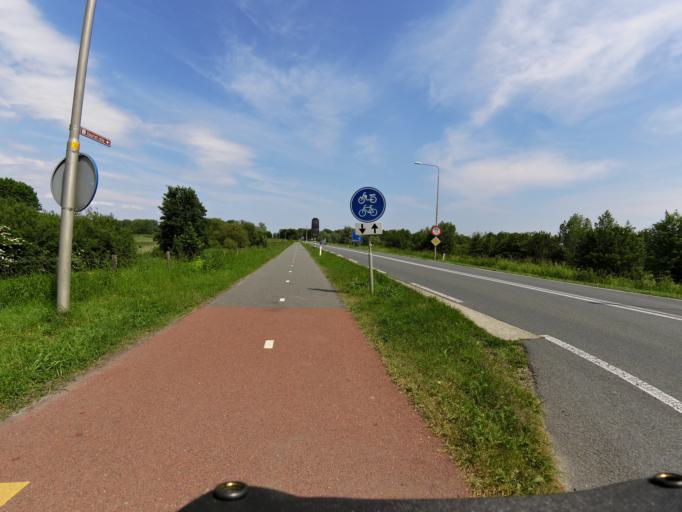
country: NL
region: North Brabant
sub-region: Gemeente Woudrichem
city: Woudrichem
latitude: 51.7967
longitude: 5.0558
